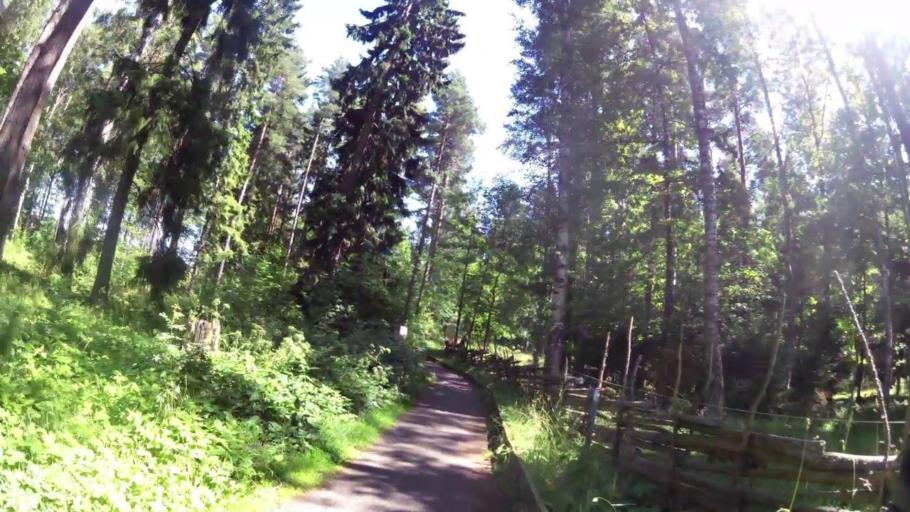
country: SE
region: OEstergoetland
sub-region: Linkopings Kommun
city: Linkoping
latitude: 58.4042
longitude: 15.5907
